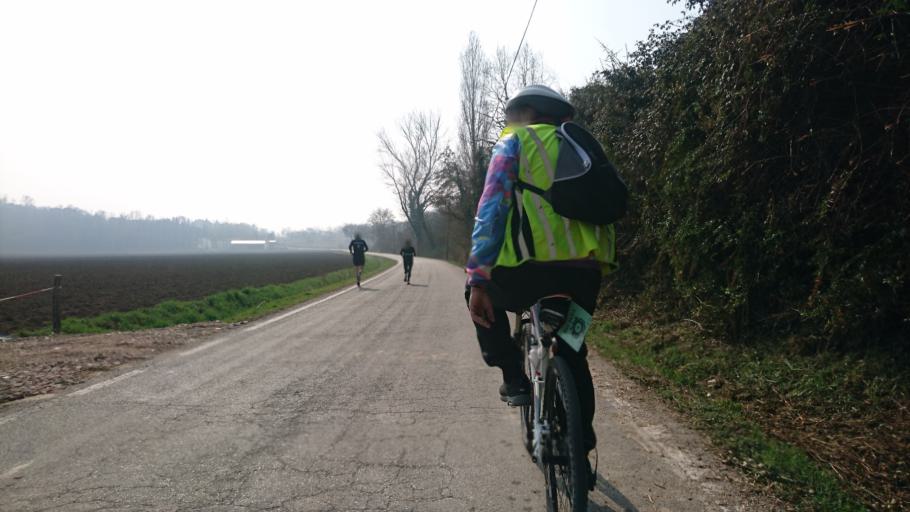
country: IT
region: Veneto
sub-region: Provincia di Vicenza
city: Montegalda
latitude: 45.4601
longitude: 11.6681
